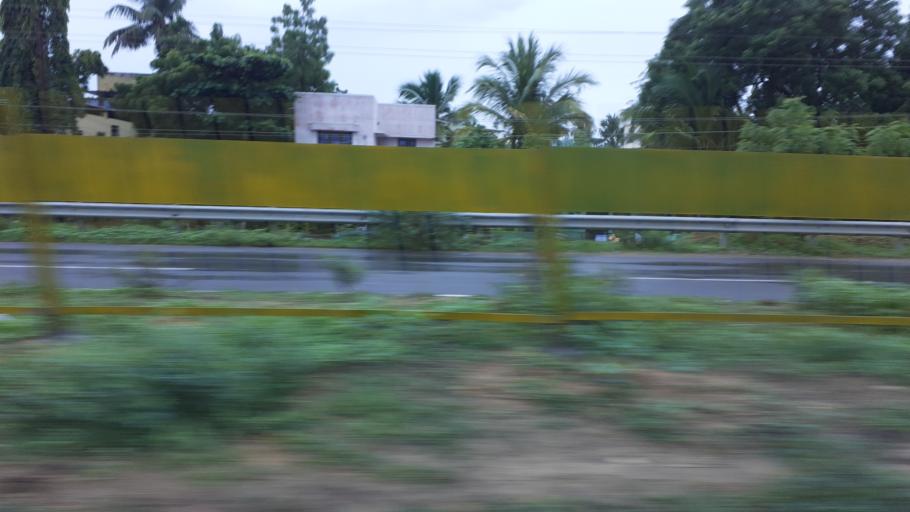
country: IN
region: Tamil Nadu
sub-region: Tirunelveli Kattabo
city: Tirunelveli
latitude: 8.7138
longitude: 77.7748
